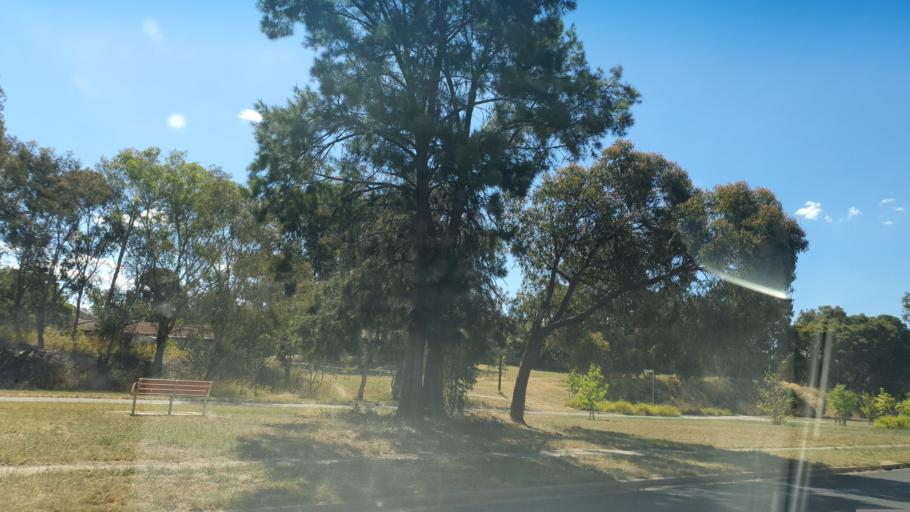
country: AU
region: Australian Capital Territory
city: Macquarie
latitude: -35.2342
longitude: 149.0625
